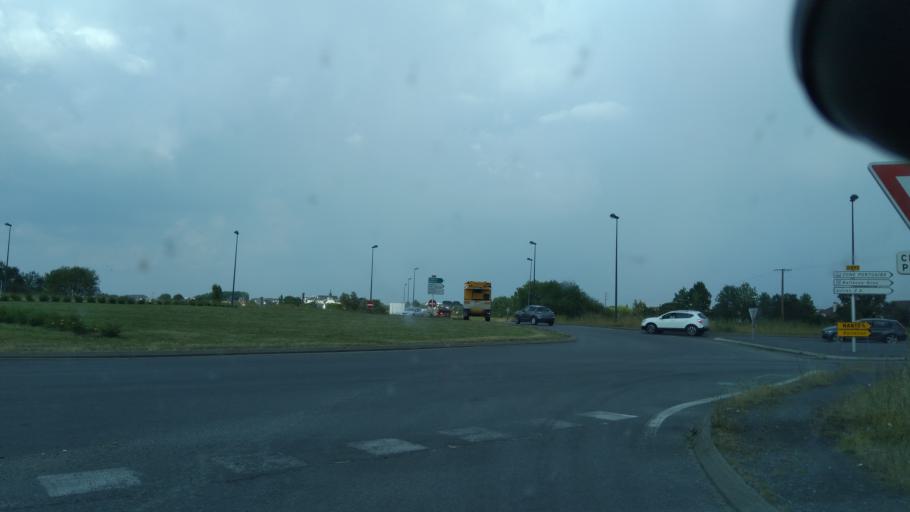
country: FR
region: Pays de la Loire
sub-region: Departement de la Loire-Atlantique
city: Montoir-de-Bretagne
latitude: 47.3219
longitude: -2.1655
